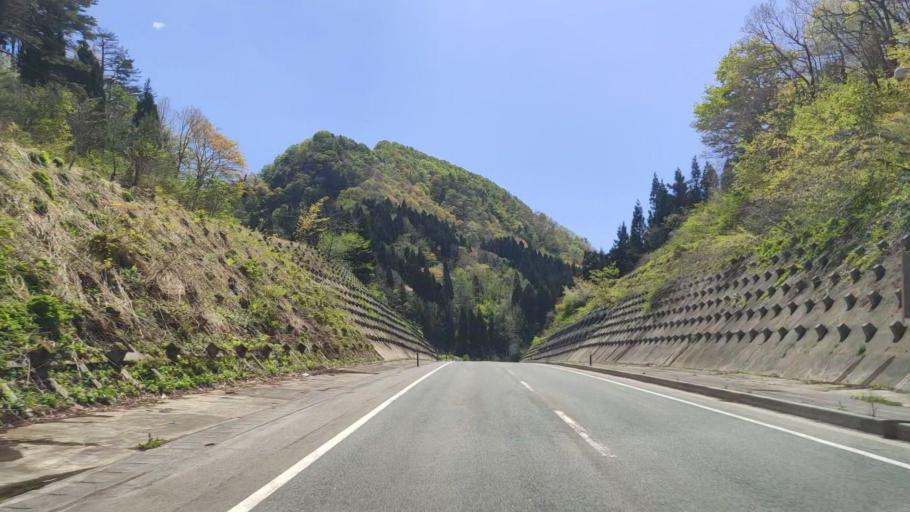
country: JP
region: Yamagata
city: Shinjo
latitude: 38.9001
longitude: 140.3276
